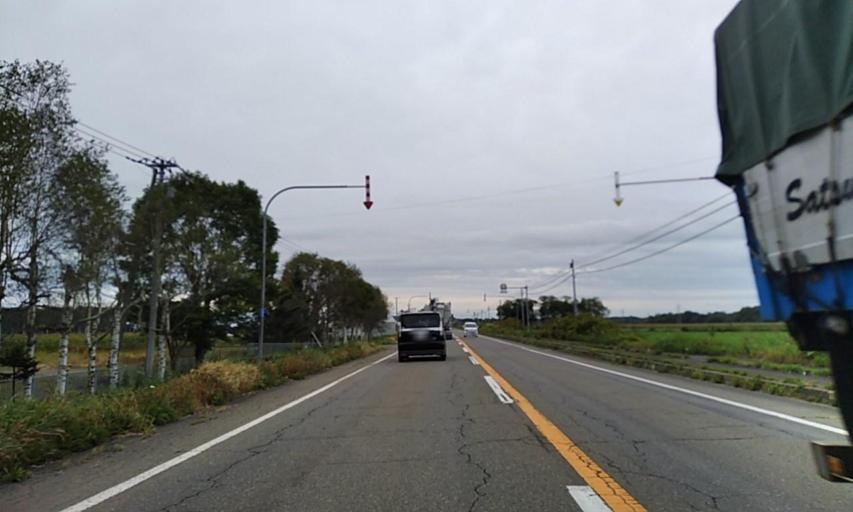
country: JP
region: Hokkaido
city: Obihiro
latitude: 42.4623
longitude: 143.2794
